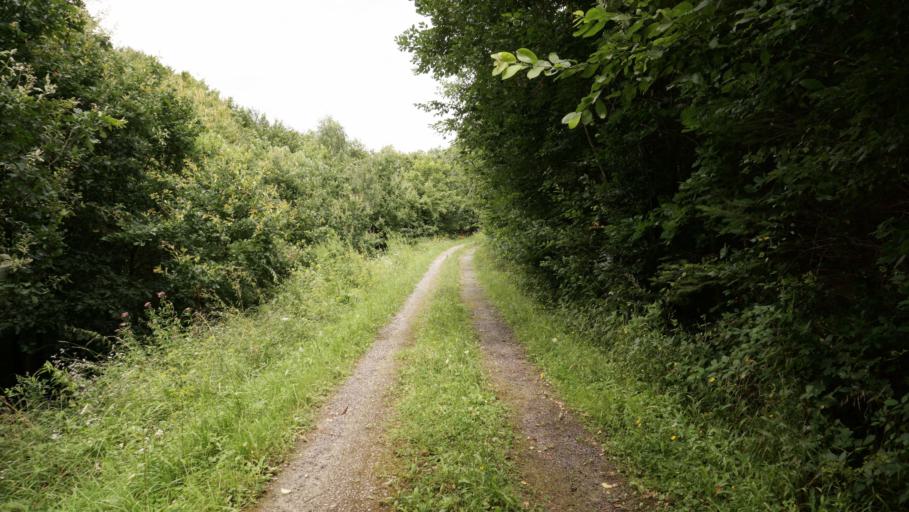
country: DE
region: Baden-Wuerttemberg
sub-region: Karlsruhe Region
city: Neckarzimmern
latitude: 49.3213
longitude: 9.1516
